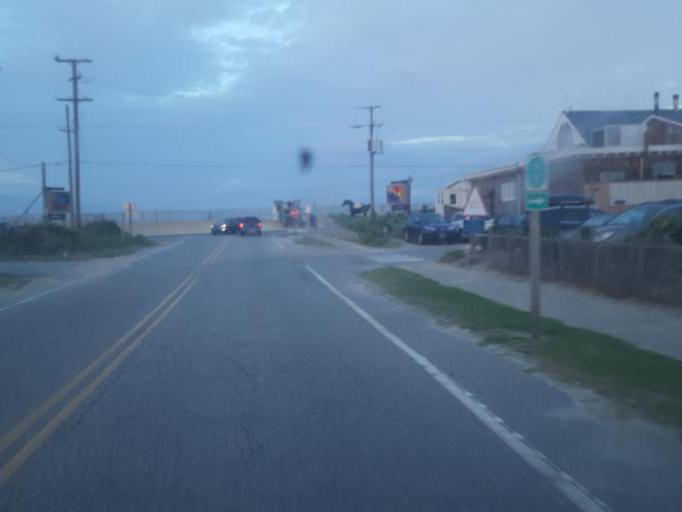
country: US
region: North Carolina
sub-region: Dare County
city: Kitty Hawk
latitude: 36.0671
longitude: -75.6914
